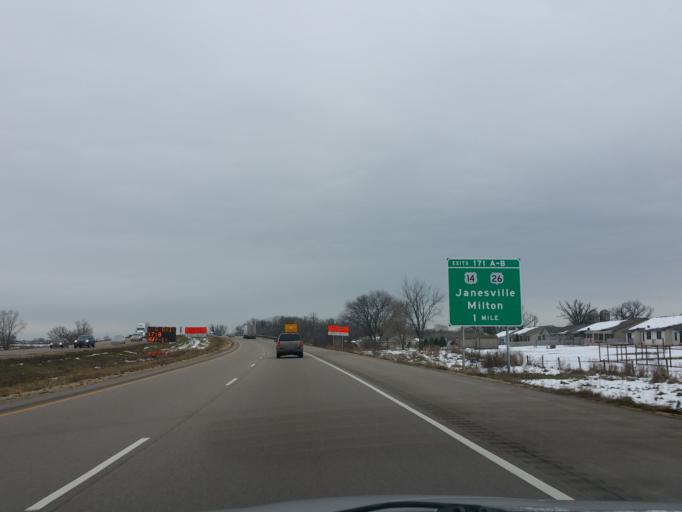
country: US
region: Wisconsin
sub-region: Rock County
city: Janesville
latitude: 42.7408
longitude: -89.0056
